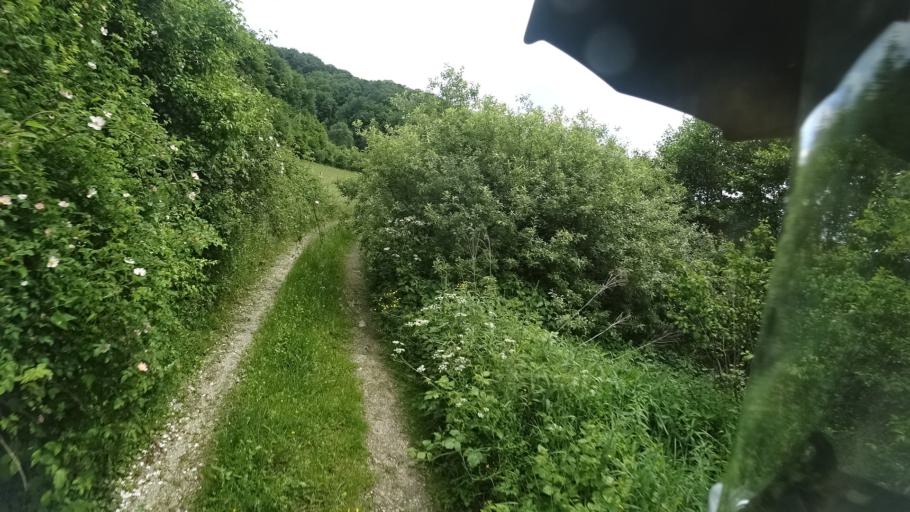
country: HR
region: Karlovacka
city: Vojnic
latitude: 45.2249
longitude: 15.6318
